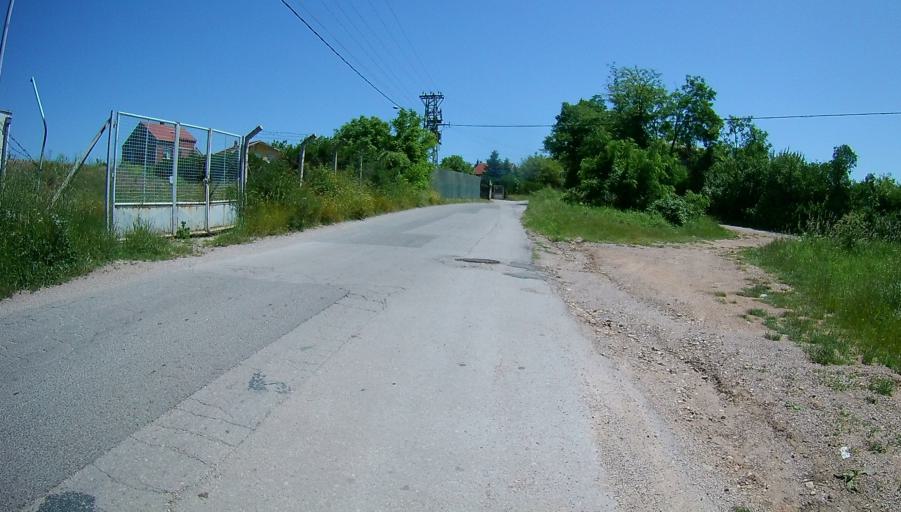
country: RS
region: Central Serbia
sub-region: Nisavski Okrug
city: Nis
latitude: 43.2938
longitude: 21.8997
